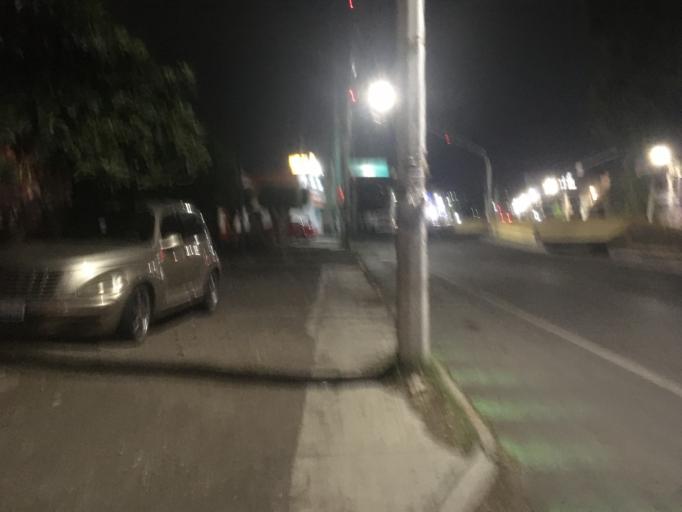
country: MX
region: Queretaro
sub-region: Queretaro
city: Santiago de Queretaro
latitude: 20.6131
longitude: -100.4002
